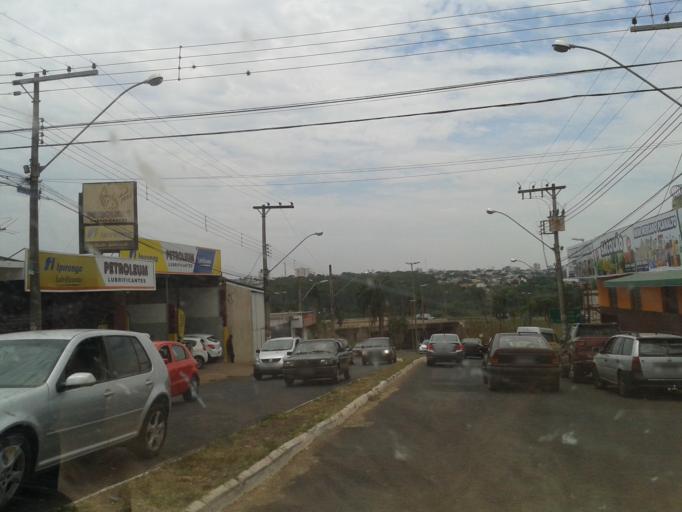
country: BR
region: Minas Gerais
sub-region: Uberlandia
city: Uberlandia
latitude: -18.9092
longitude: -48.3144
